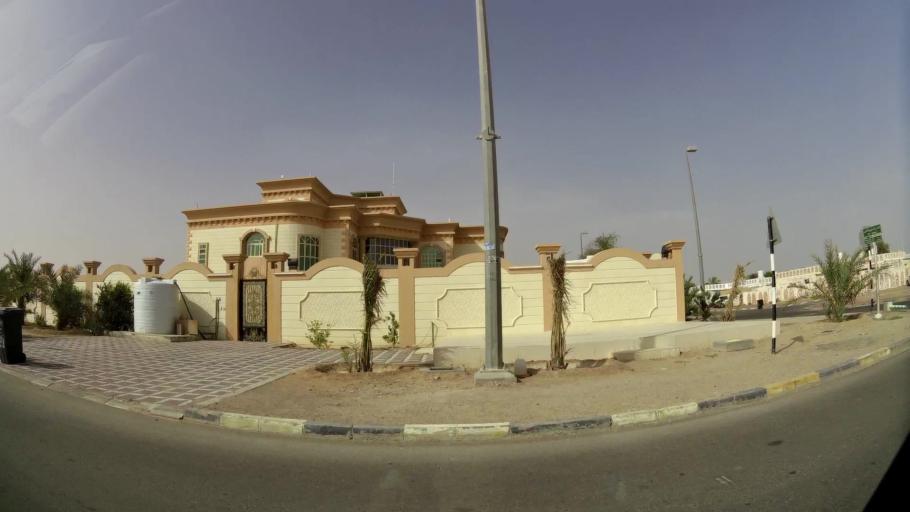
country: AE
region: Abu Dhabi
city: Al Ain
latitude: 24.2137
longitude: 55.5833
